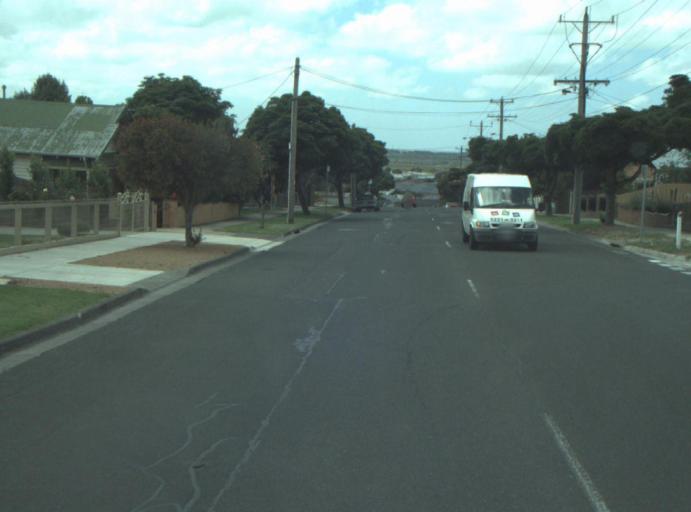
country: AU
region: Victoria
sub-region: Greater Geelong
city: Breakwater
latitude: -38.1738
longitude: 144.3453
